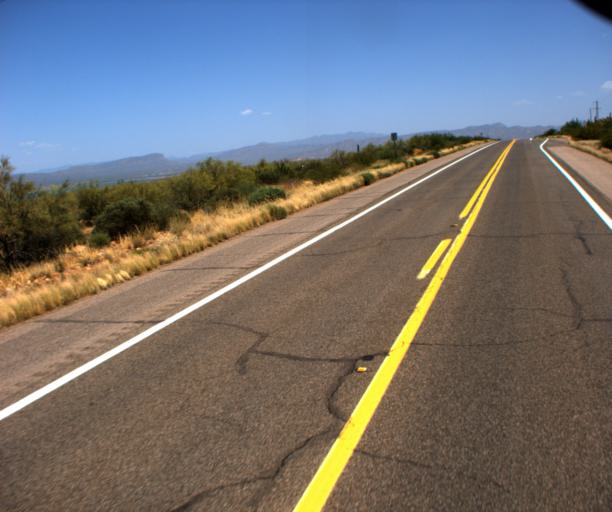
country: US
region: Arizona
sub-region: Gila County
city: Tonto Basin
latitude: 33.6557
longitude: -111.1080
